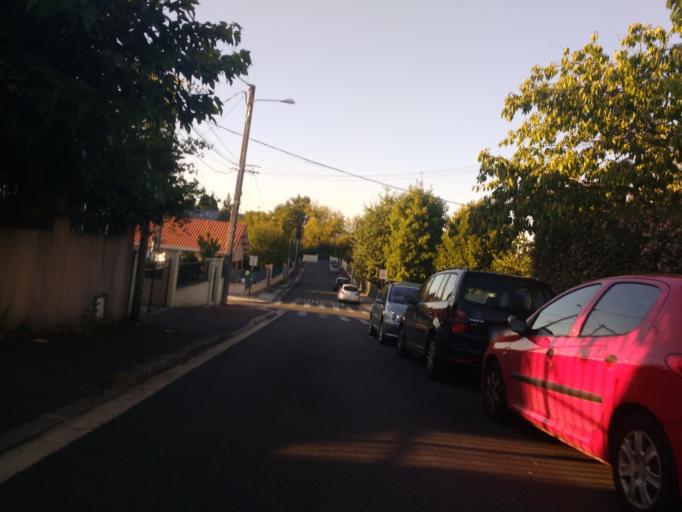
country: FR
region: Aquitaine
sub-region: Departement de la Gironde
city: Pessac
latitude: 44.8137
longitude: -0.6289
